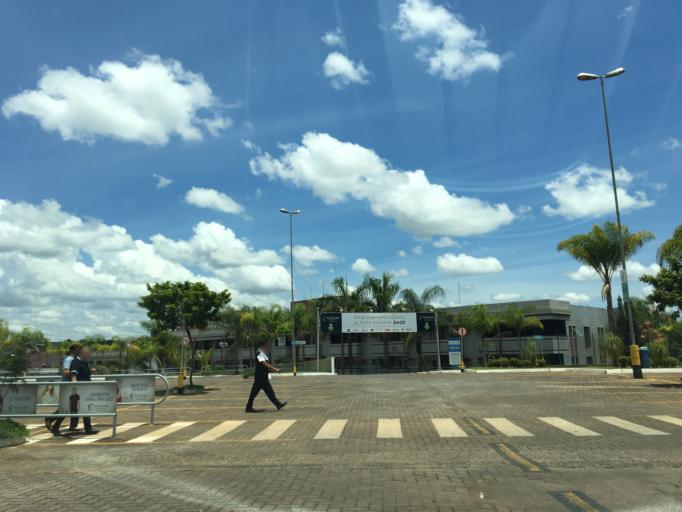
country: BR
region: Federal District
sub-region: Brasilia
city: Brasilia
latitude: -15.7345
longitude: -47.8983
